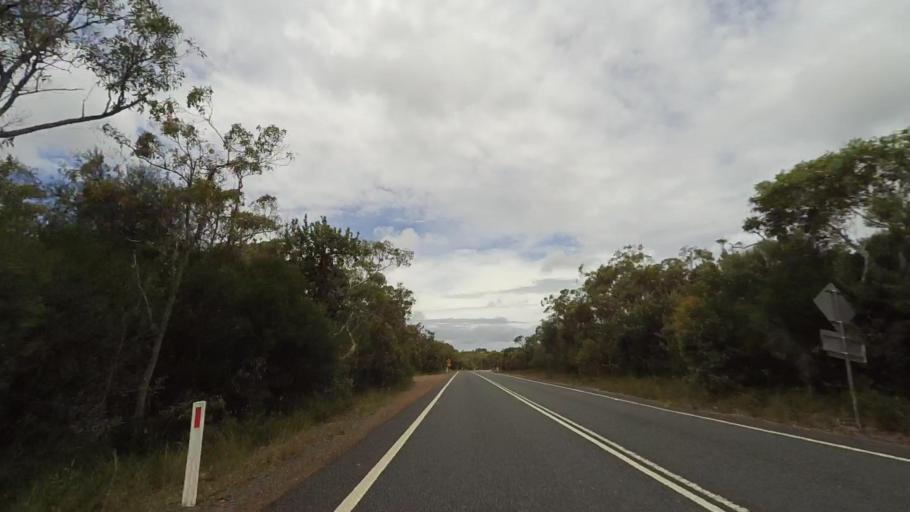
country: AU
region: New South Wales
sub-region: Sutherland Shire
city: Heathcote
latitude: -34.1046
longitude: 151.0590
